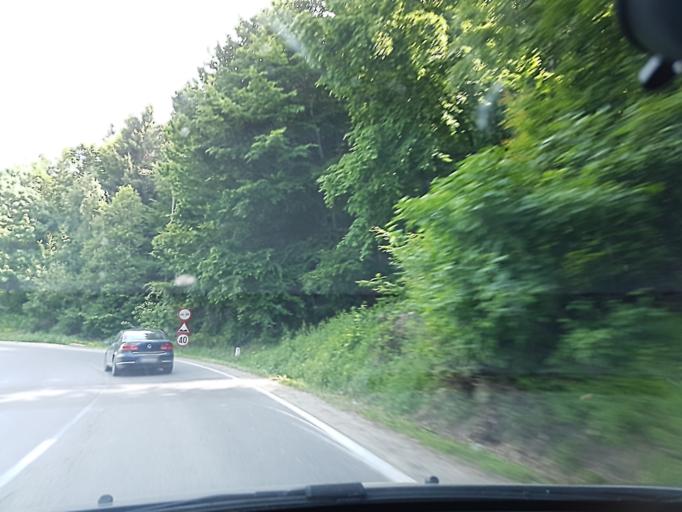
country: RO
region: Prahova
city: Maneciu
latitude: 45.3400
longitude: 25.9565
